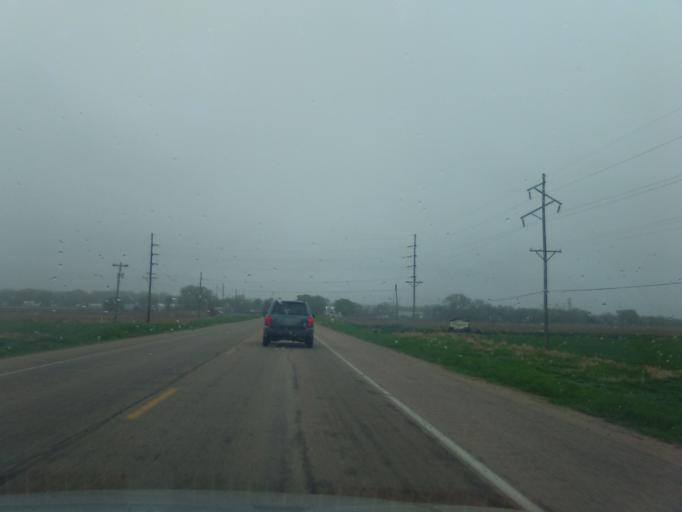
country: US
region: Nebraska
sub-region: Wayne County
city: Wayne
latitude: 42.2199
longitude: -97.0178
